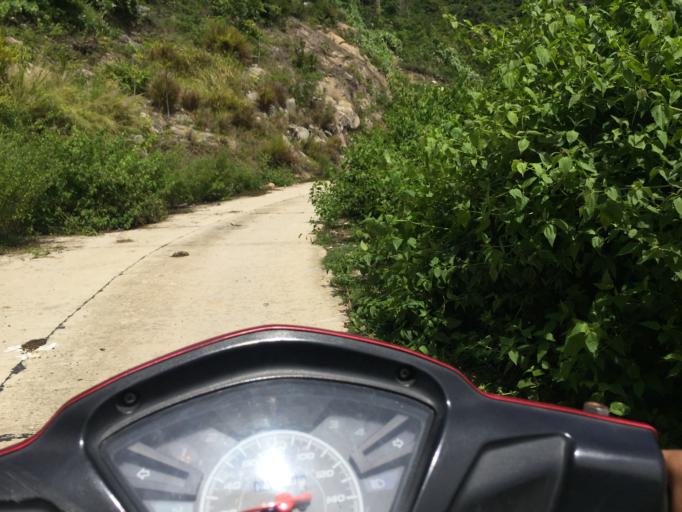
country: VN
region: Quang Nam
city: Hoi An
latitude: 15.9713
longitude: 108.5063
